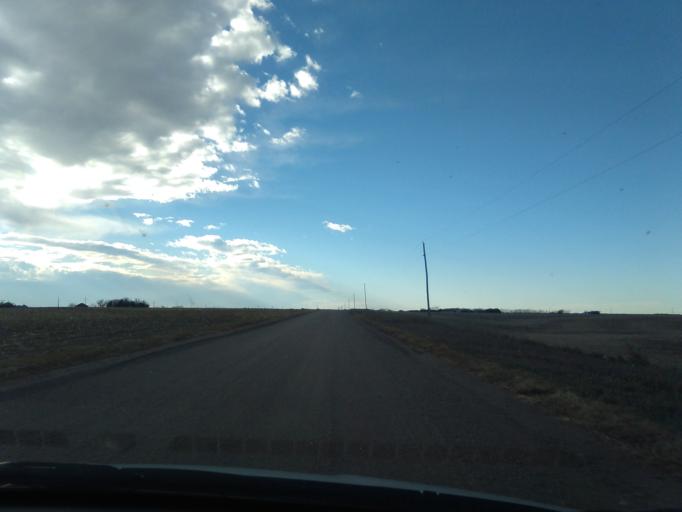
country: US
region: Nebraska
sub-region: Kearney County
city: Minden
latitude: 40.3649
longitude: -98.8248
